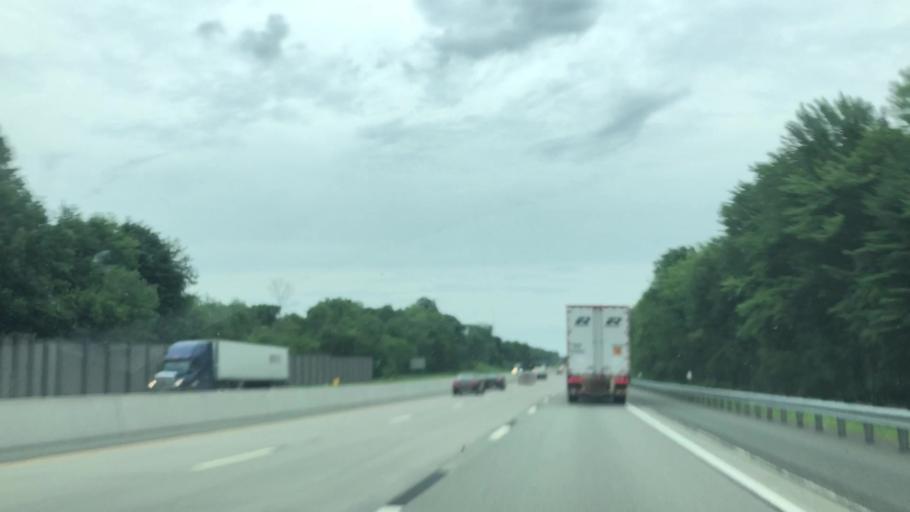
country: US
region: New York
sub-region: Albany County
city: McKownville
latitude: 42.6707
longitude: -73.8391
